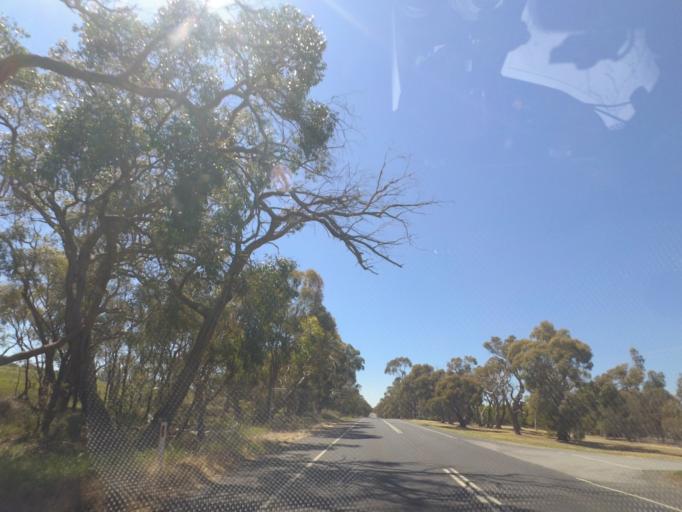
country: AU
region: Victoria
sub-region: Hume
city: Sunbury
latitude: -37.4400
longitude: 144.7054
